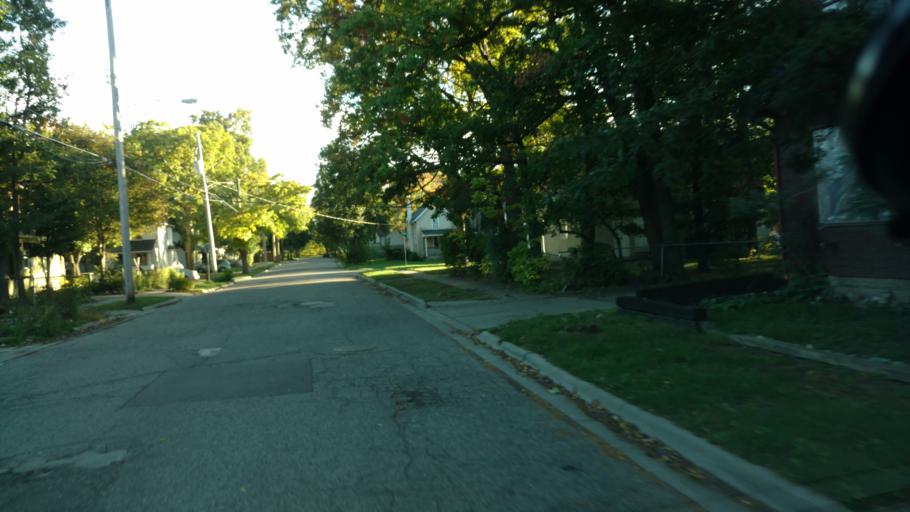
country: US
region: Michigan
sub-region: Ingham County
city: Lansing
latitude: 42.7295
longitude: -84.5349
